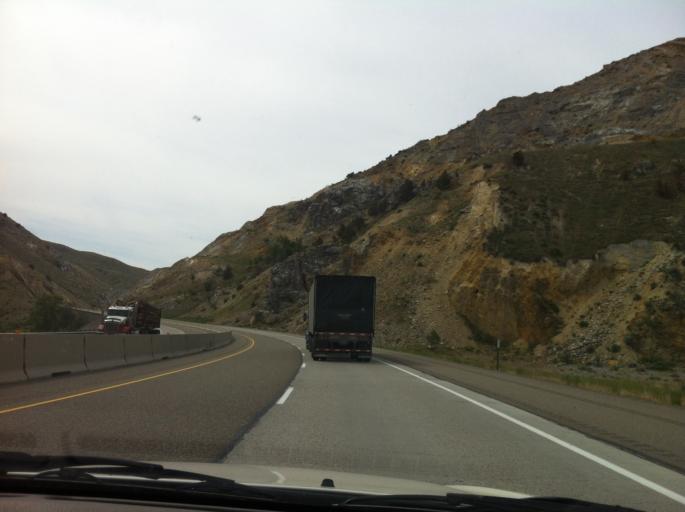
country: US
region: Idaho
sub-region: Washington County
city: Weiser
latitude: 44.4061
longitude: -117.3129
